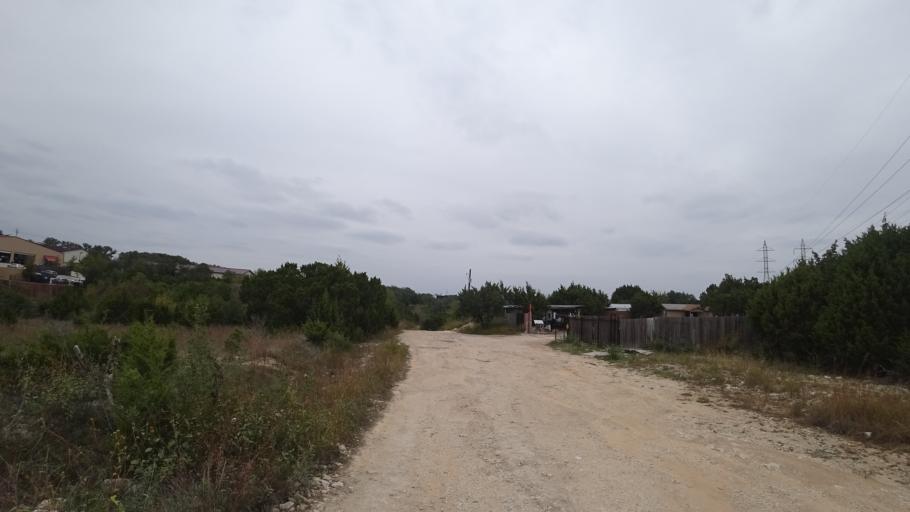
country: US
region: Texas
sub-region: Travis County
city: Lakeway
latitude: 30.3770
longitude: -97.9441
